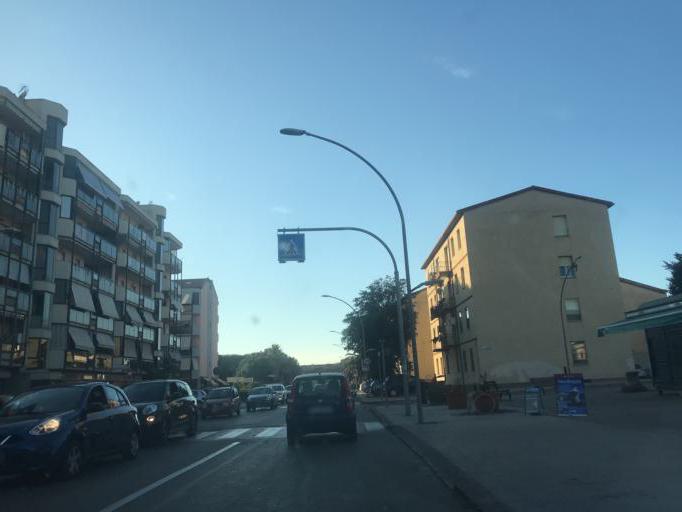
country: IT
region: Sardinia
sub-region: Provincia di Sassari
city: Alghero
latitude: 40.5762
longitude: 8.3205
